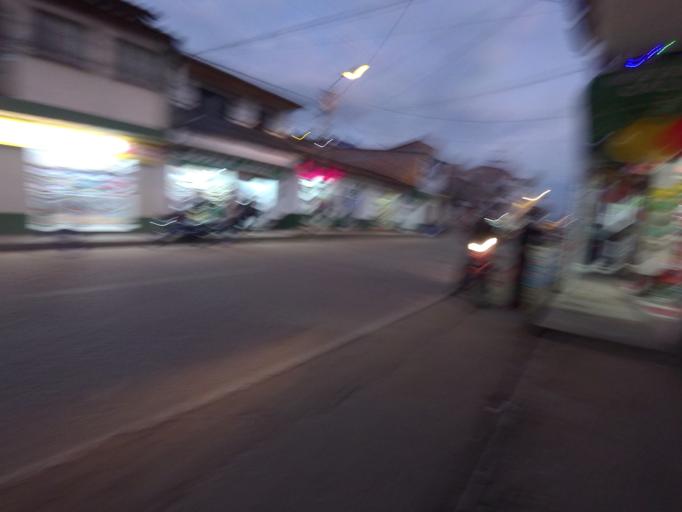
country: CO
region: Huila
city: San Agustin
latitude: 1.8810
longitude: -76.2703
